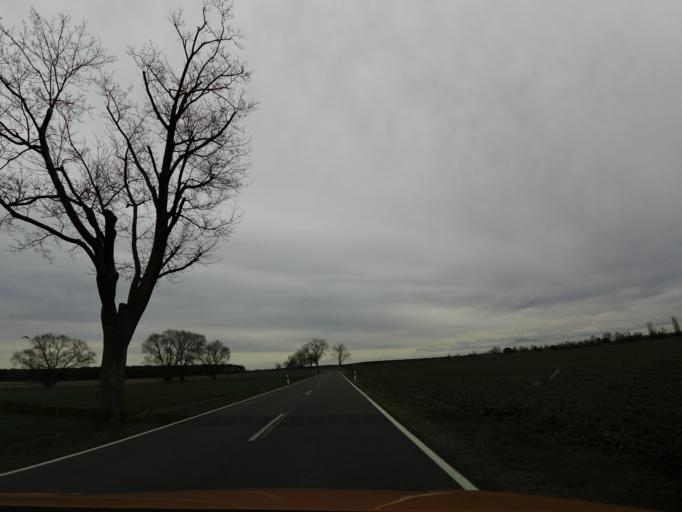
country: DE
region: Brandenburg
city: Belzig
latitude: 52.1477
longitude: 12.6646
